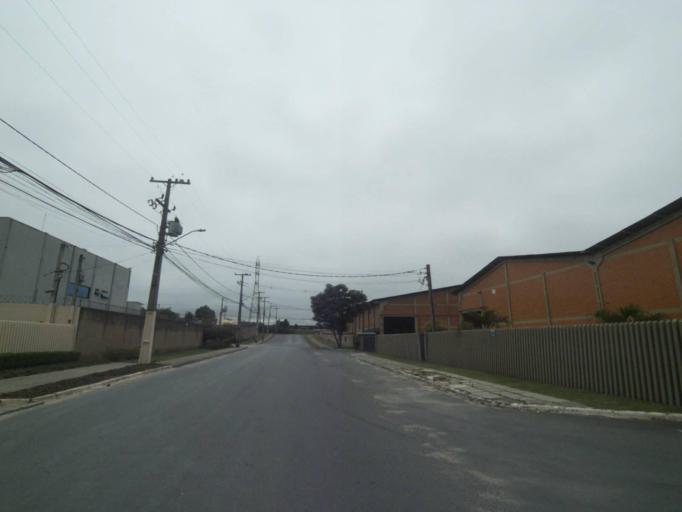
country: BR
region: Parana
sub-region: Araucaria
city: Araucaria
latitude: -25.5494
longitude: -49.3304
